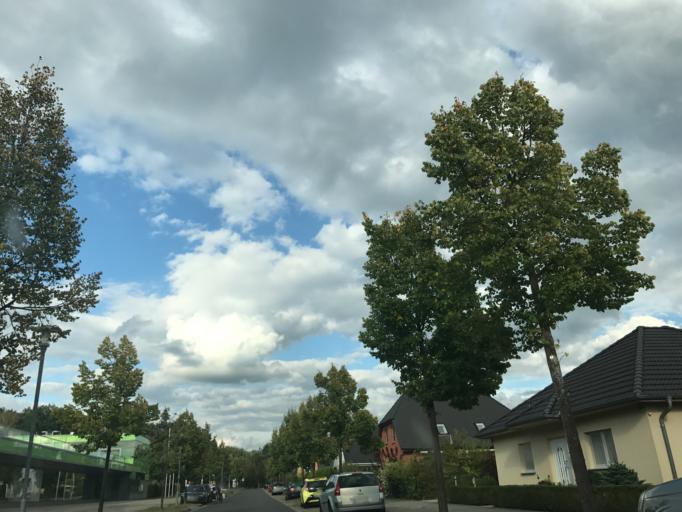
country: DE
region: Brandenburg
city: Dallgow-Doeberitz
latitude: 52.5410
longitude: 13.0455
